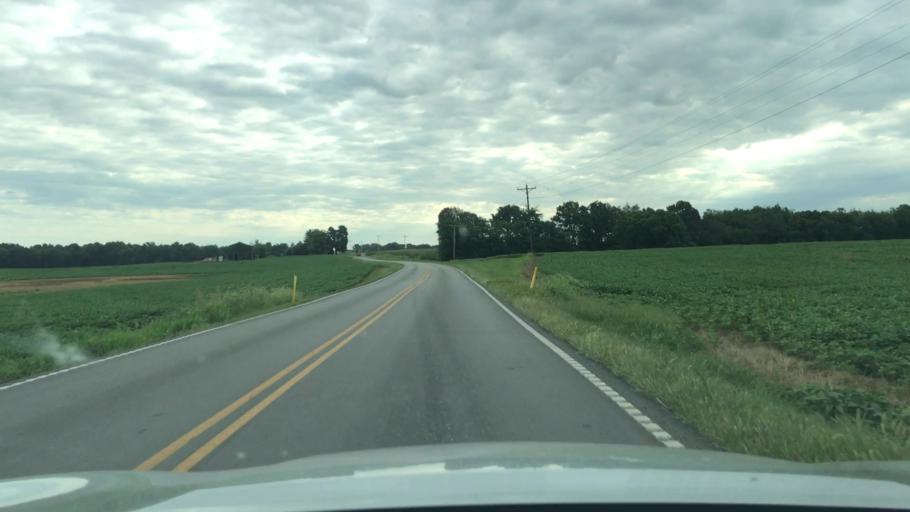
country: US
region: Kentucky
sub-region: Todd County
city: Elkton
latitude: 36.7413
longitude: -87.1810
